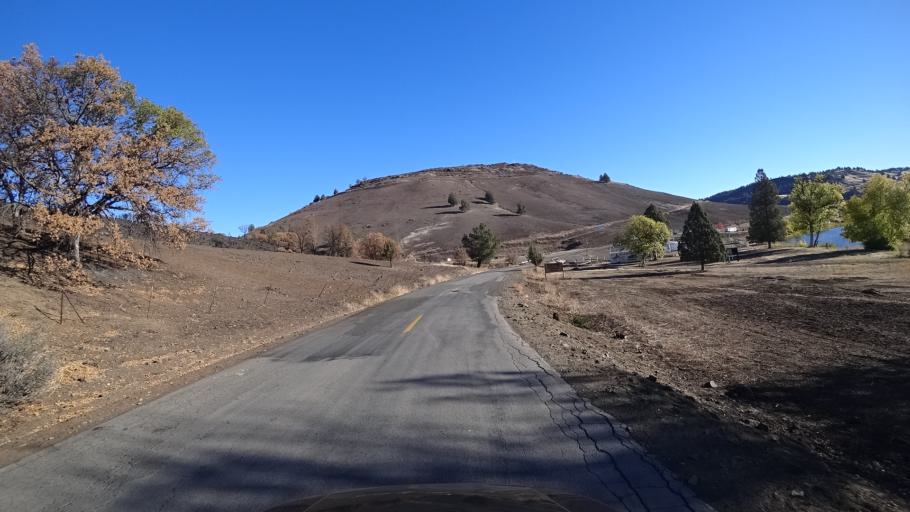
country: US
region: California
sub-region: Siskiyou County
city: Montague
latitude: 41.9167
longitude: -122.4615
